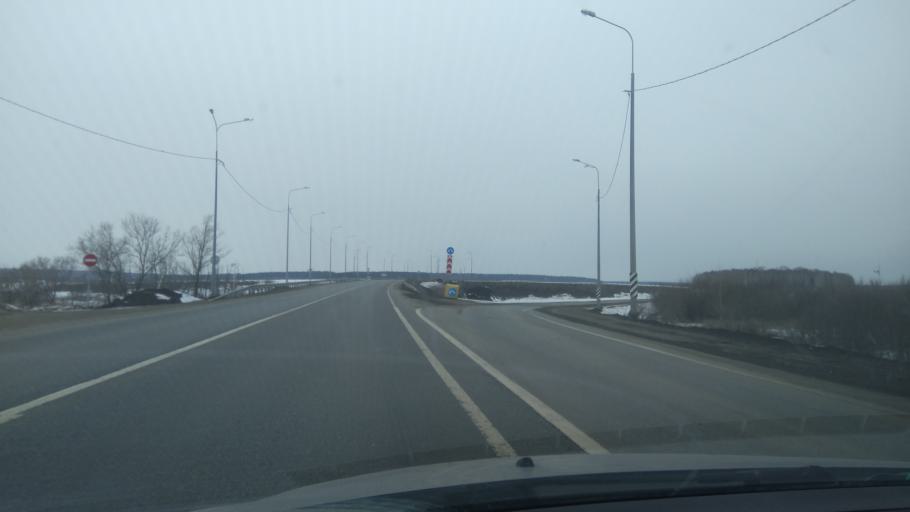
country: RU
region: Sverdlovsk
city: Achit
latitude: 56.7869
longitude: 57.8868
